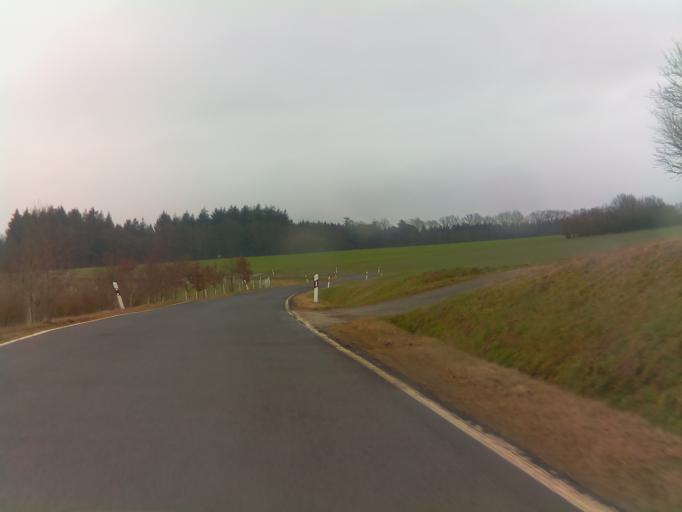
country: DE
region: Rheinland-Pfalz
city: Dill
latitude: 49.9165
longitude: 7.3526
